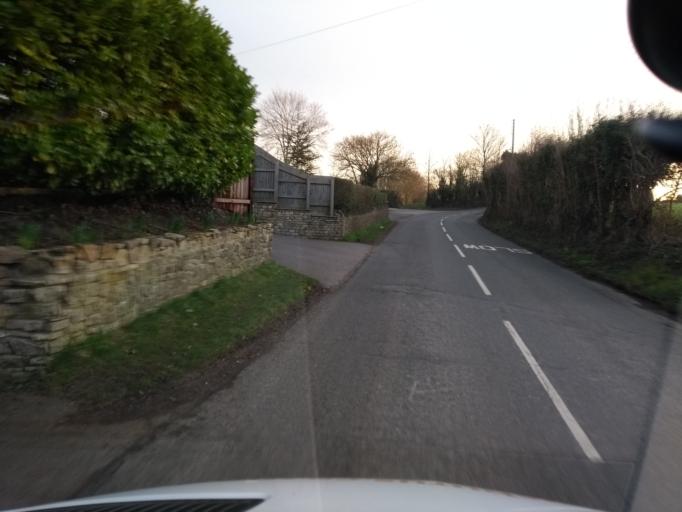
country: GB
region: England
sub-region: Somerset
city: Wedmore
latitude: 51.2248
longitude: -2.8098
